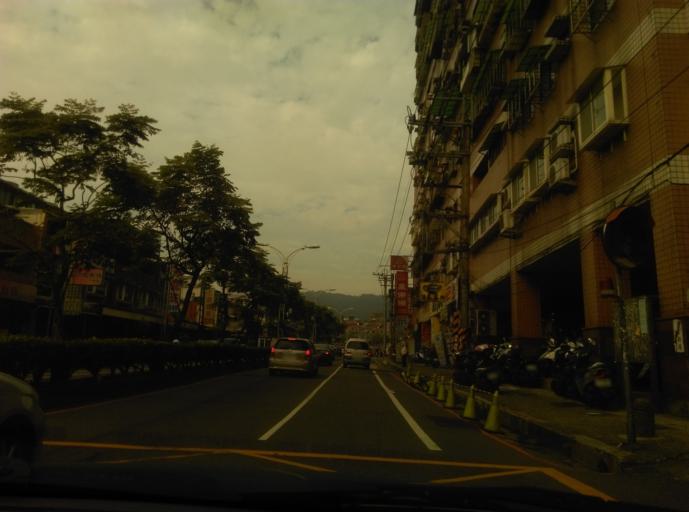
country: TW
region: Taiwan
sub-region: Keelung
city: Keelung
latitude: 25.1537
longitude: 121.6972
